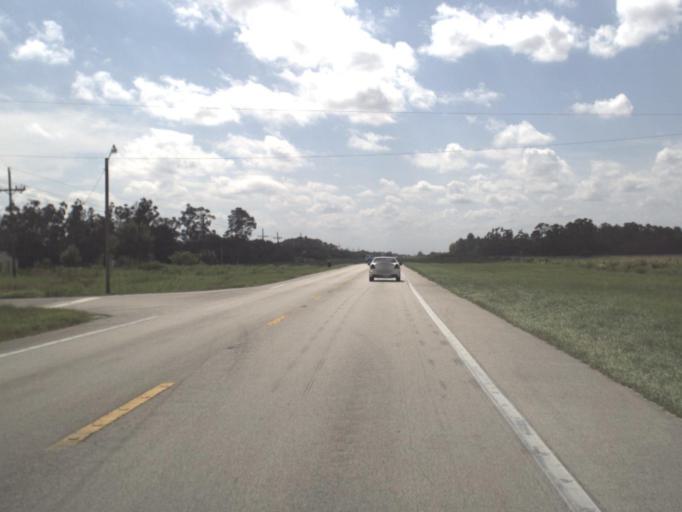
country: US
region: Florida
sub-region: Hendry County
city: Port LaBelle
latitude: 26.6649
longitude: -81.4363
